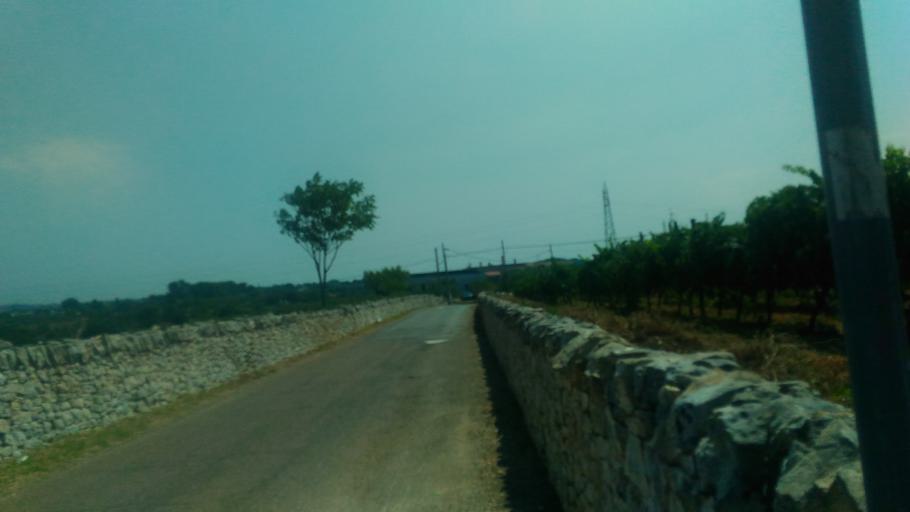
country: IT
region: Apulia
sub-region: Provincia di Brindisi
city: Cisternino
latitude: 40.7448
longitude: 17.3792
